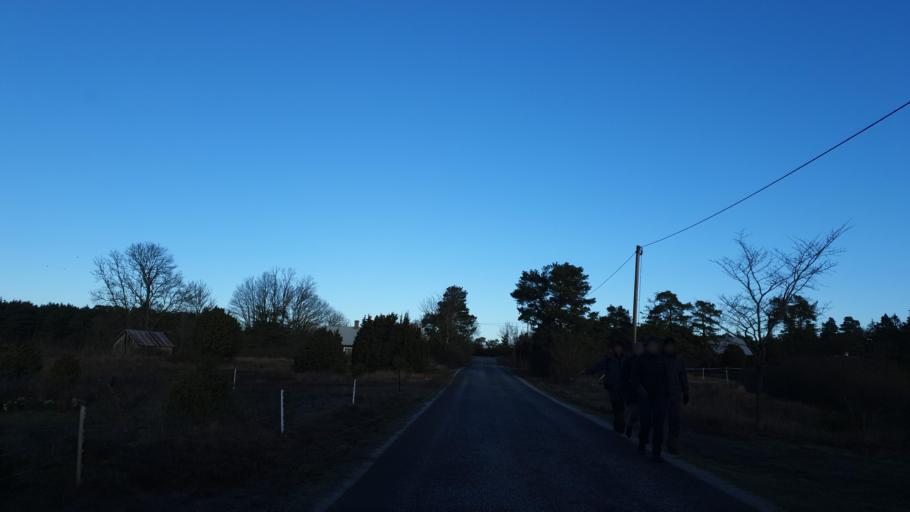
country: SE
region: Gotland
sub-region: Gotland
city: Slite
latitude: 57.3889
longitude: 18.8088
